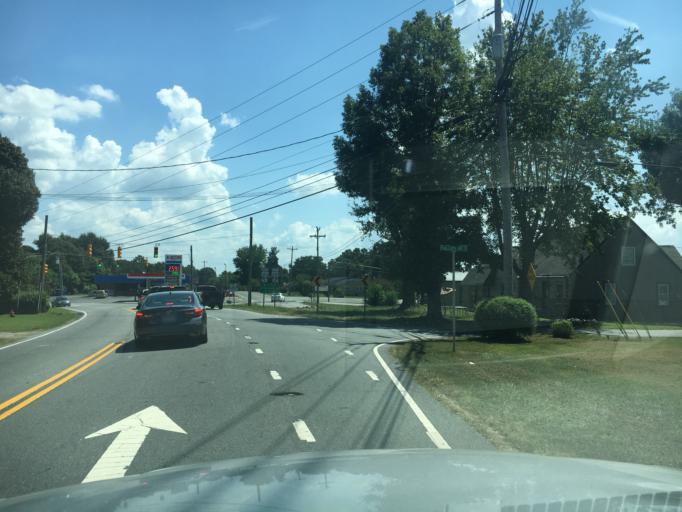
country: US
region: North Carolina
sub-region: Rutherford County
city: Forest City
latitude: 35.2898
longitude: -81.8448
